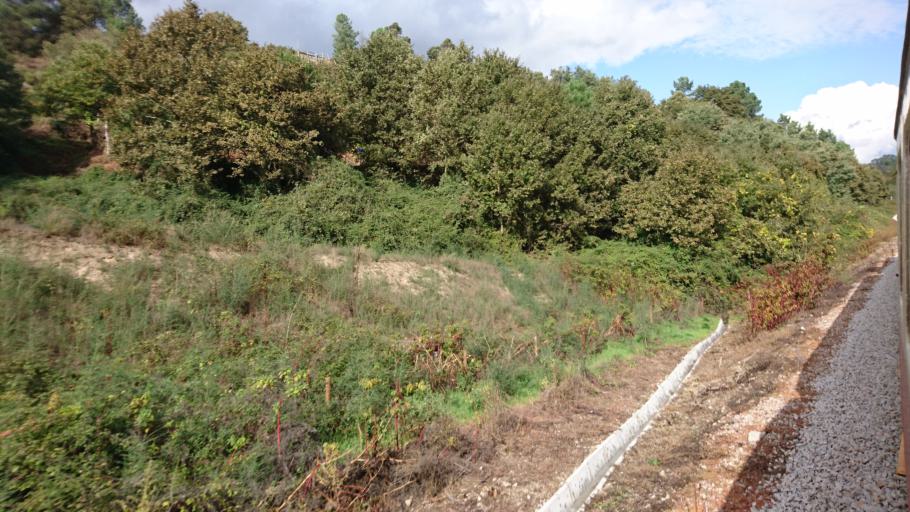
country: PT
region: Porto
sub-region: Marco de Canaveses
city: Marco de Canavezes
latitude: 41.1906
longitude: -8.1396
